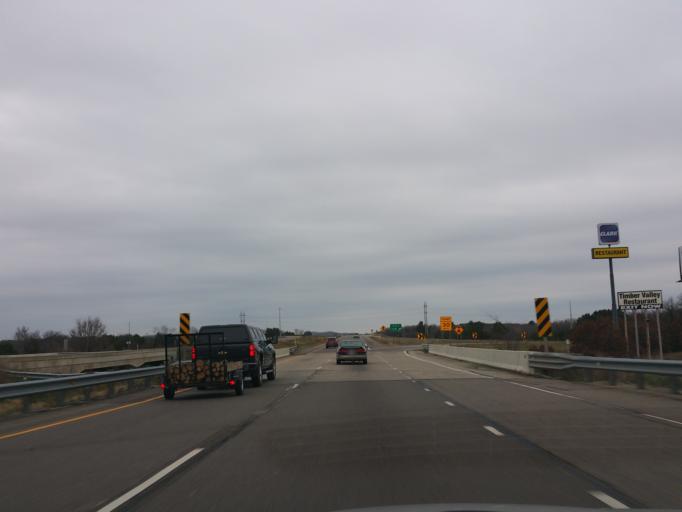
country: US
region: Wisconsin
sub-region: Jackson County
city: Black River Falls
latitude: 44.3889
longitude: -91.0069
